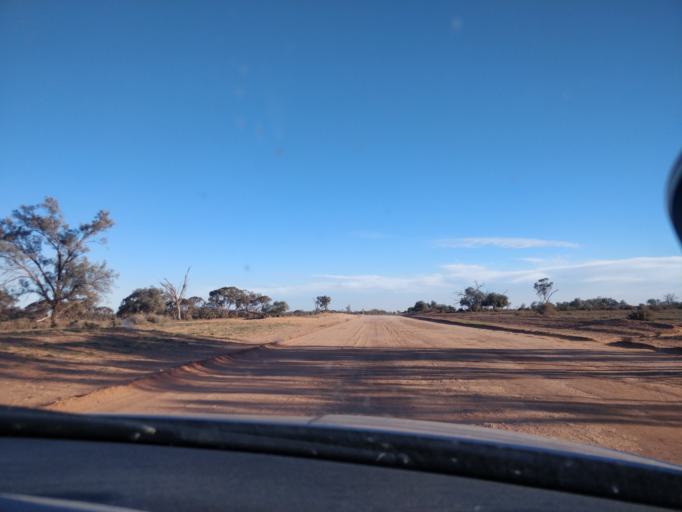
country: AU
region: New South Wales
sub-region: Wentworth
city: Gol Gol
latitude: -33.8837
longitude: 142.8788
